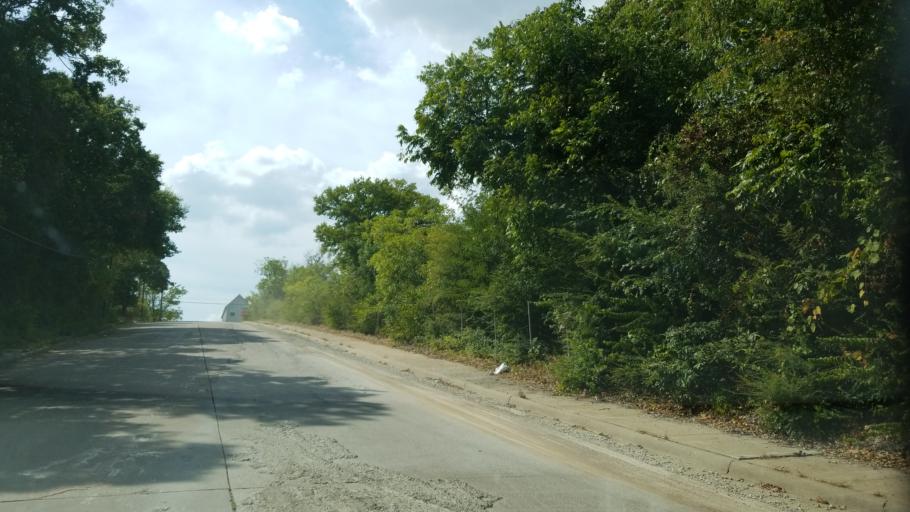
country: US
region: Texas
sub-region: Dallas County
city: Dallas
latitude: 32.7714
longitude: -96.8379
